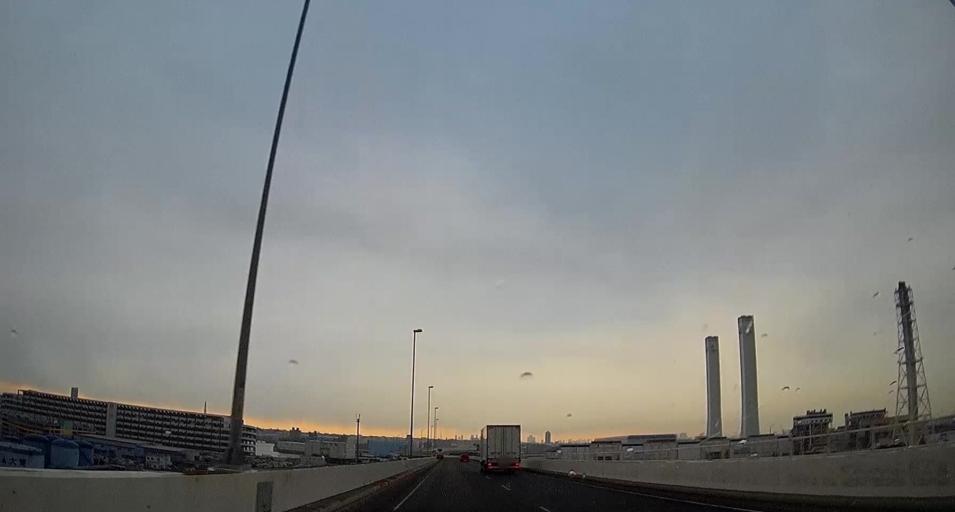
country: JP
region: Kanagawa
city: Yokohama
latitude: 35.4692
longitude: 139.6765
